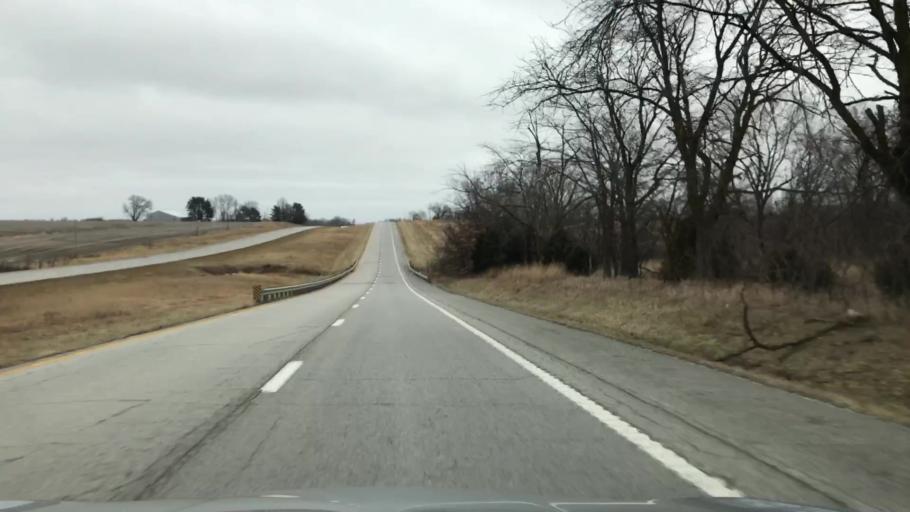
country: US
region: Missouri
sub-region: Linn County
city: Brookfield
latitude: 39.7785
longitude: -93.1627
